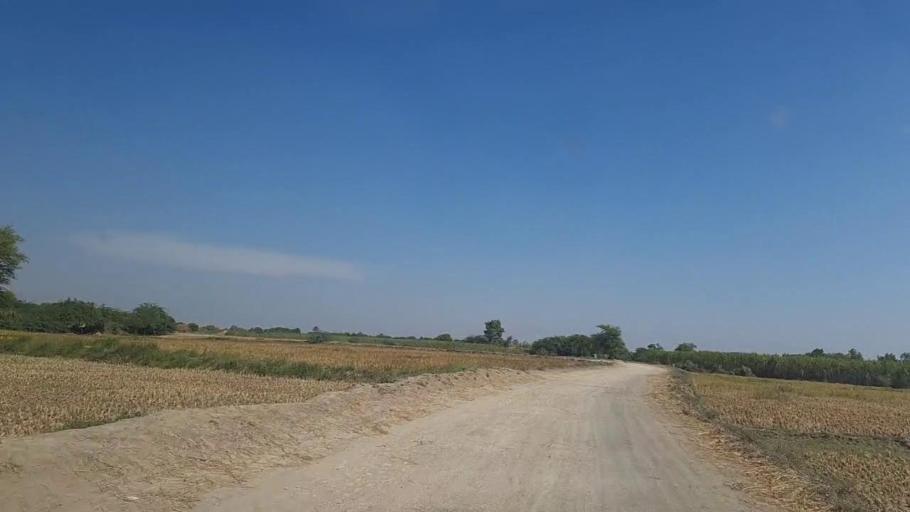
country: PK
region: Sindh
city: Mirpur Batoro
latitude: 24.7479
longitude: 68.2806
